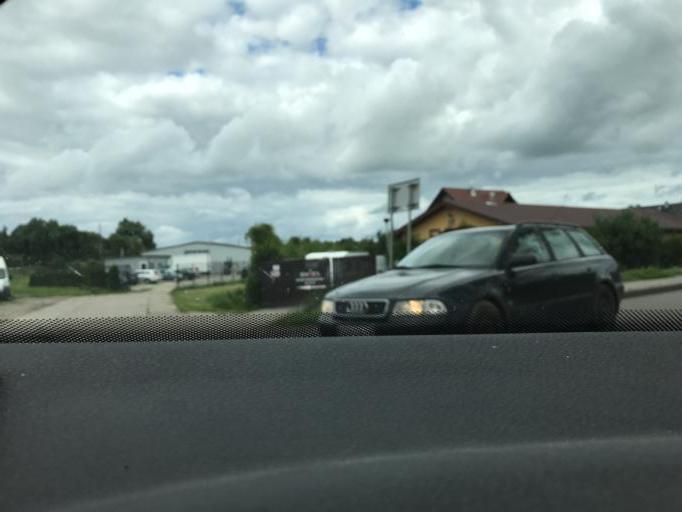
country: PL
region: Pomeranian Voivodeship
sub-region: Powiat gdanski
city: Pruszcz Gdanski
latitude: 54.2697
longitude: 18.6762
